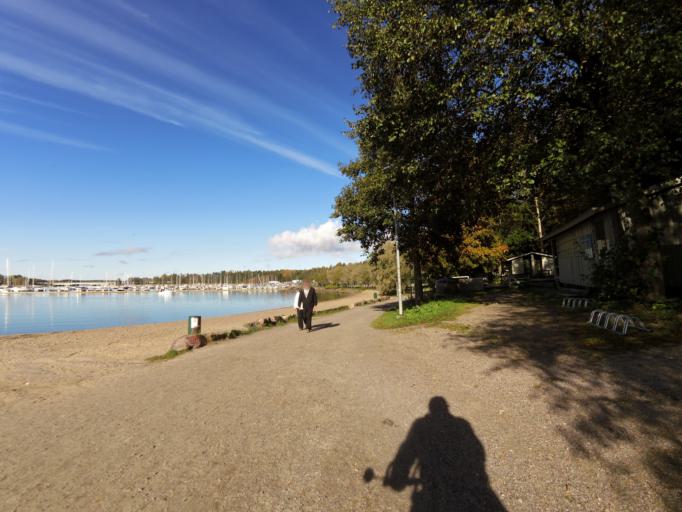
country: FI
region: Uusimaa
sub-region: Helsinki
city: Espoo
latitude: 60.1532
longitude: 24.6266
